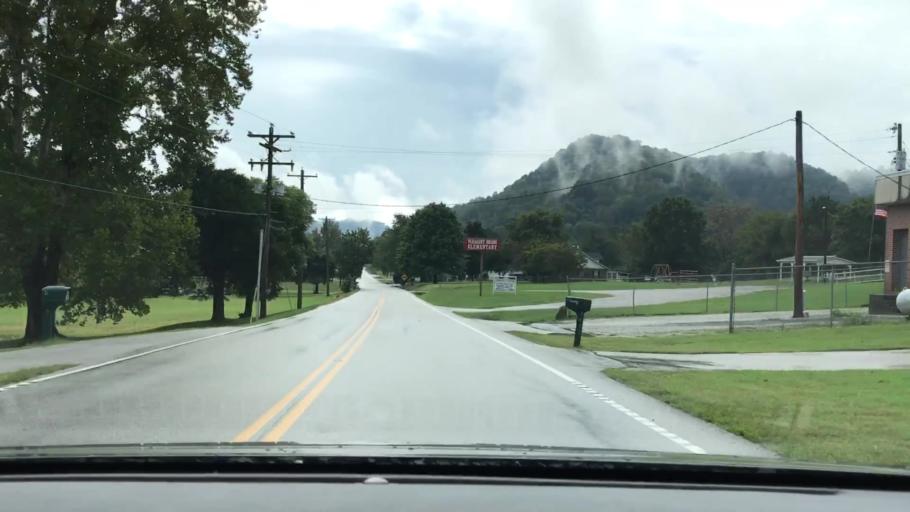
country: US
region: Tennessee
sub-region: Smith County
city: Carthage
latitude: 36.3843
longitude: -85.9489
